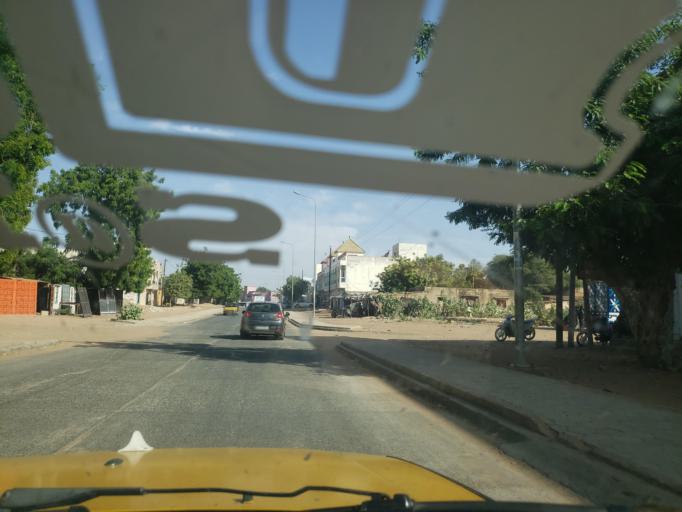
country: SN
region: Louga
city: Louga
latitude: 15.6223
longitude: -16.2125
